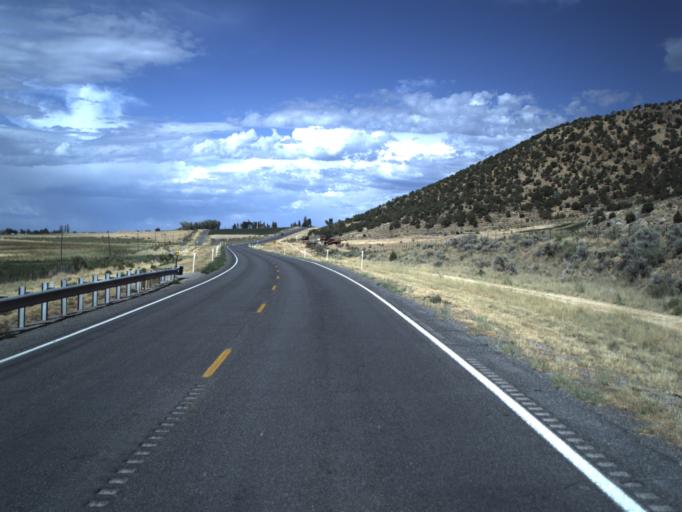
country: US
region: Utah
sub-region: Sanpete County
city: Manti
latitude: 39.2355
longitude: -111.6605
